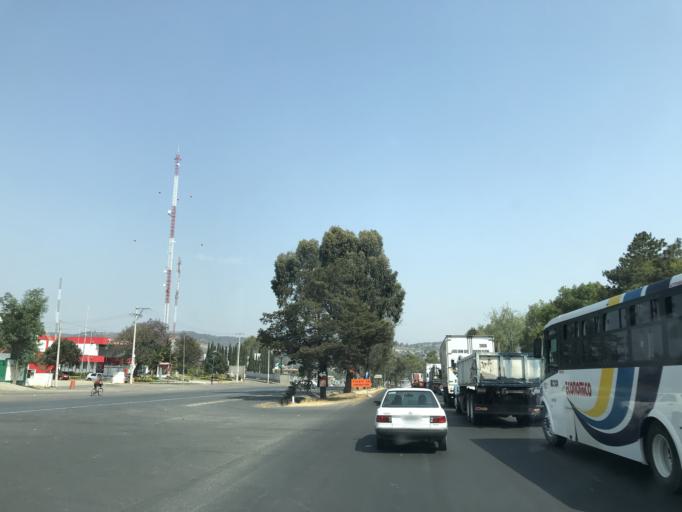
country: MX
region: Tlaxcala
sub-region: Apetatitlan de Antonio Carvajal
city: Tlatempan
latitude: 19.3350
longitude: -98.1976
